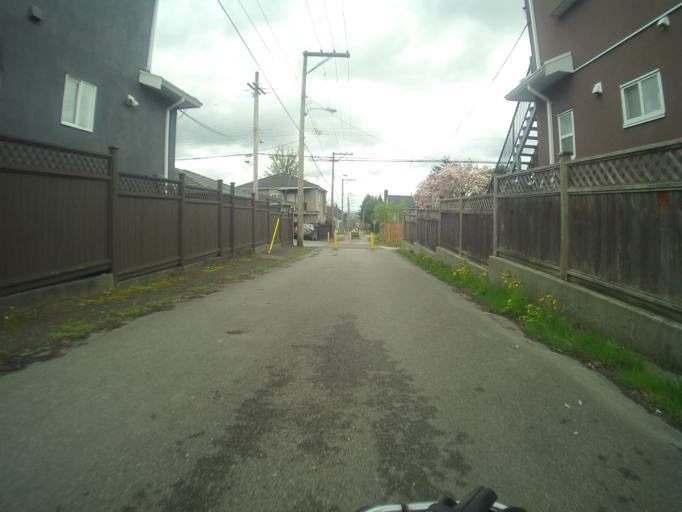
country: CA
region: British Columbia
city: Vancouver
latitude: 49.2178
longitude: -123.0741
